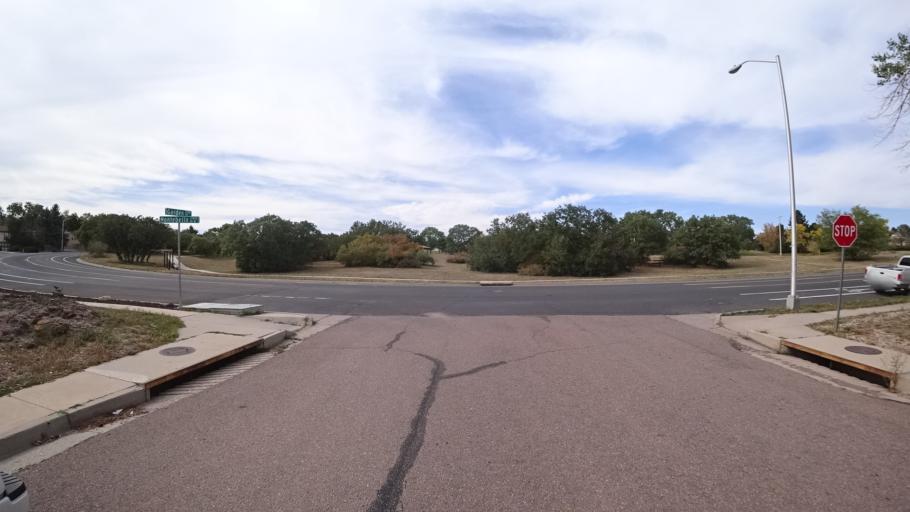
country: US
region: Colorado
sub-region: El Paso County
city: Colorado Springs
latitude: 38.9048
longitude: -104.7838
